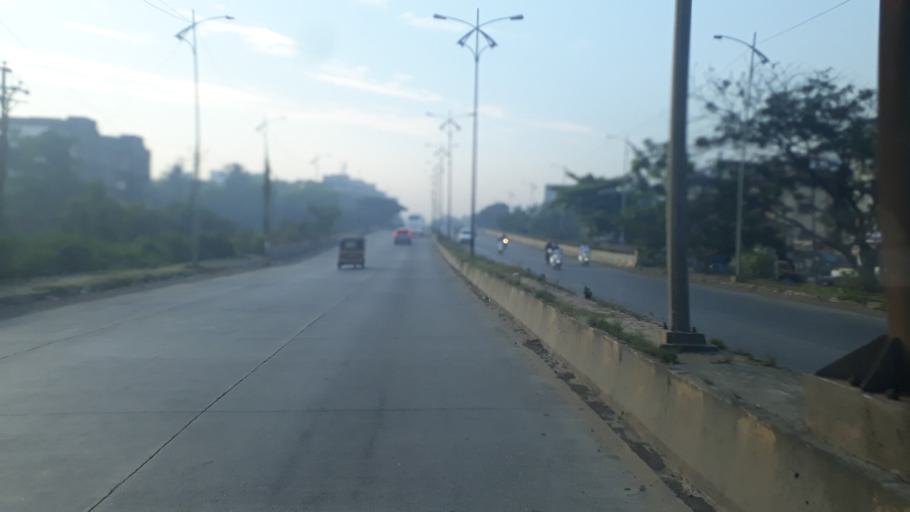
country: IN
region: Maharashtra
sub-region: Raigarh
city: Panvel
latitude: 18.9831
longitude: 73.1161
